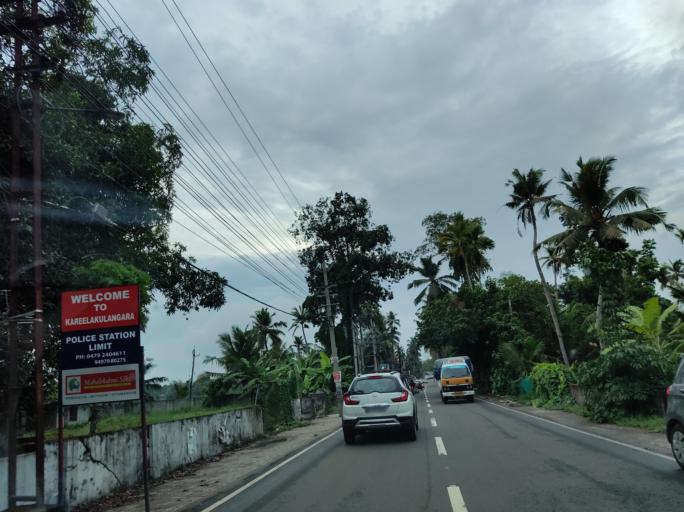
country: IN
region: Kerala
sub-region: Alappuzha
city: Mavelikara
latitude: 9.2518
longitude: 76.5031
